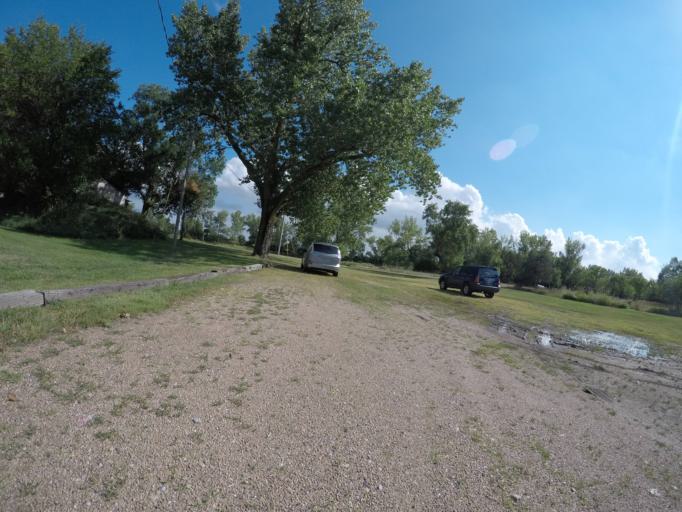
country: US
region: Nebraska
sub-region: Buffalo County
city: Kearney
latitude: 40.6560
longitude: -99.0097
